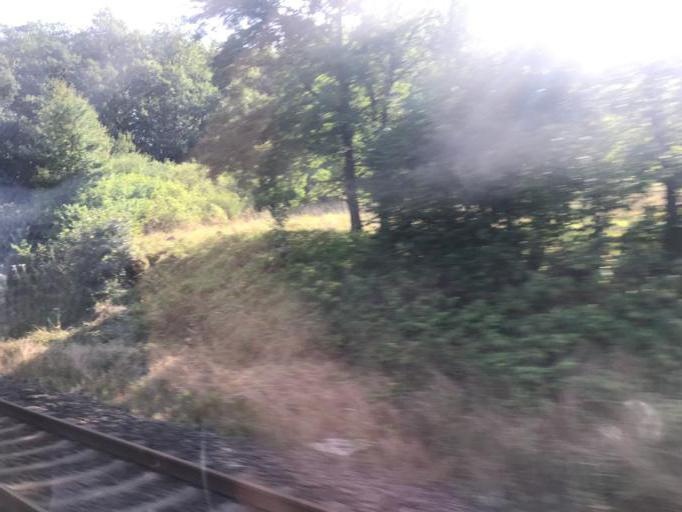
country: DE
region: Rheinland-Pfalz
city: Nohen
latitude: 49.6341
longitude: 7.2307
